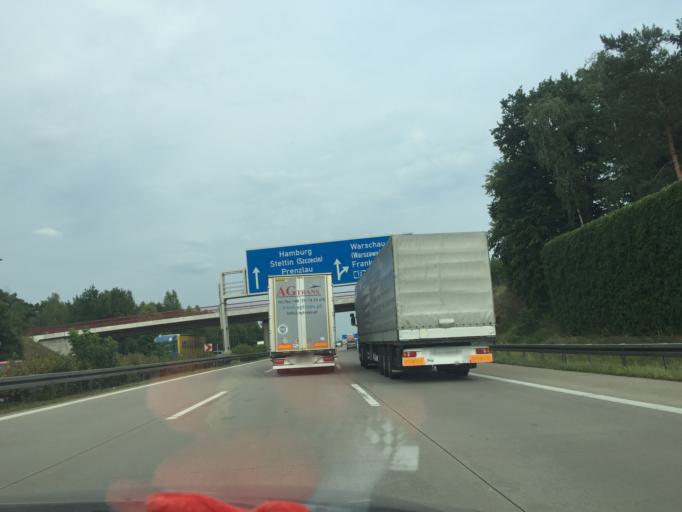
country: DE
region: Brandenburg
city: Wildau
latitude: 52.3246
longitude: 13.7155
